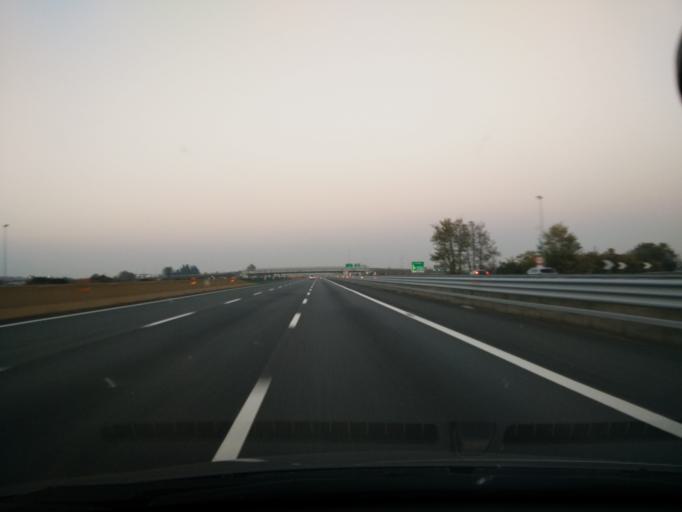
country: IT
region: Piedmont
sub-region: Provincia di Vercelli
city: Santhia
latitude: 45.3770
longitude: 8.1333
